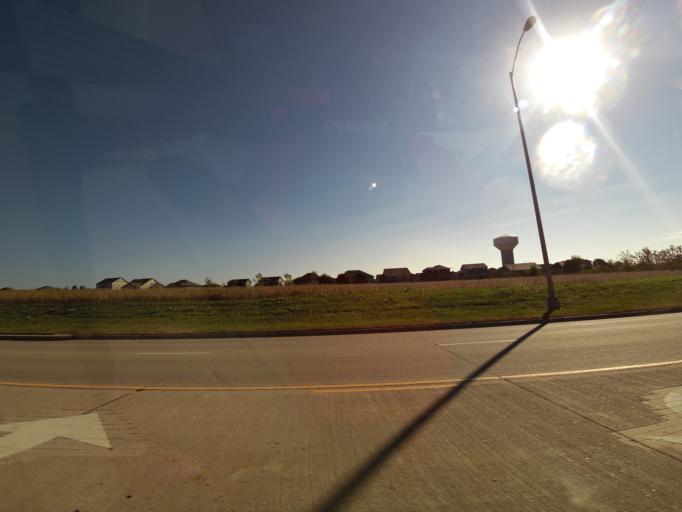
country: US
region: Nebraska
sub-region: Sarpy County
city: Gretna
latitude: 41.1268
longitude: -96.2533
